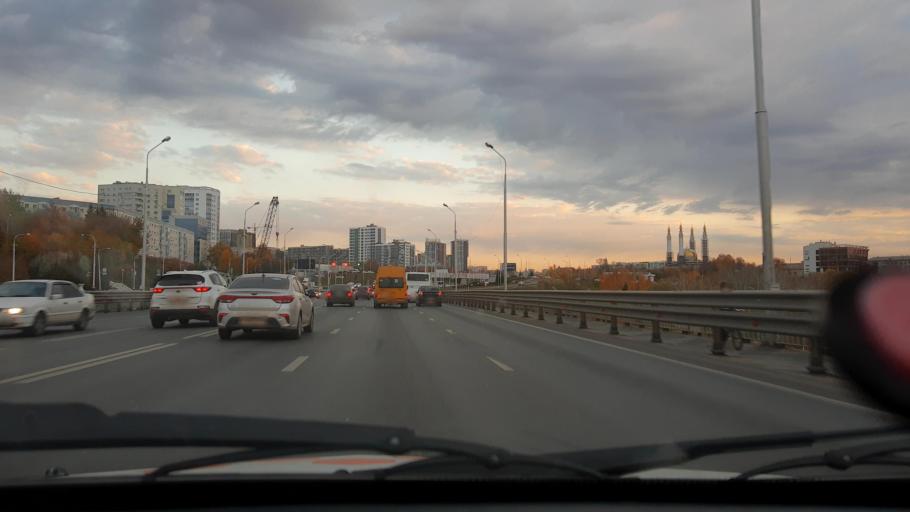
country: RU
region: Bashkortostan
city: Ufa
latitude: 54.7110
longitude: 55.9531
